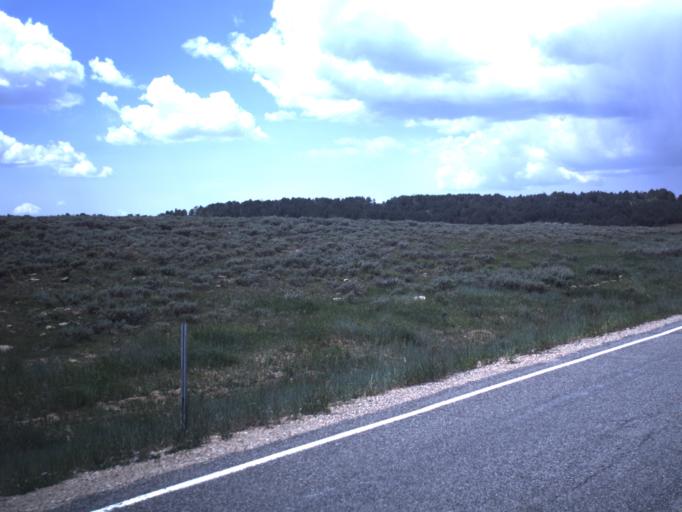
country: US
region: Utah
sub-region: Sanpete County
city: Fairview
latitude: 39.6694
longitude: -111.3067
